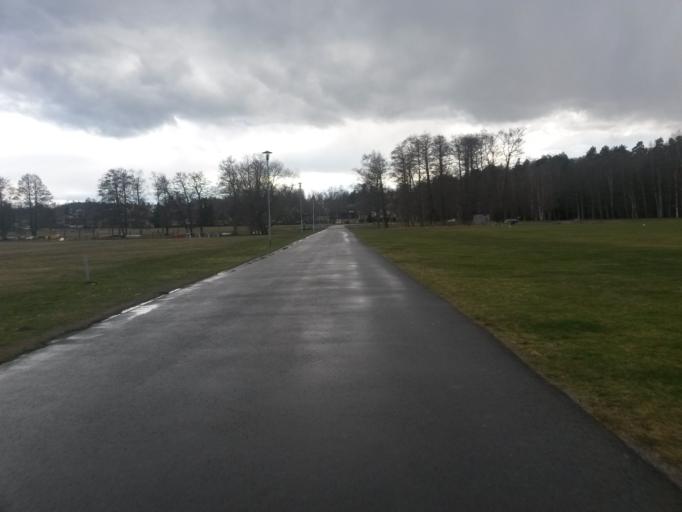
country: SE
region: OErebro
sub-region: Karlskoga Kommun
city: Karlskoga
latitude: 59.3169
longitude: 14.5156
